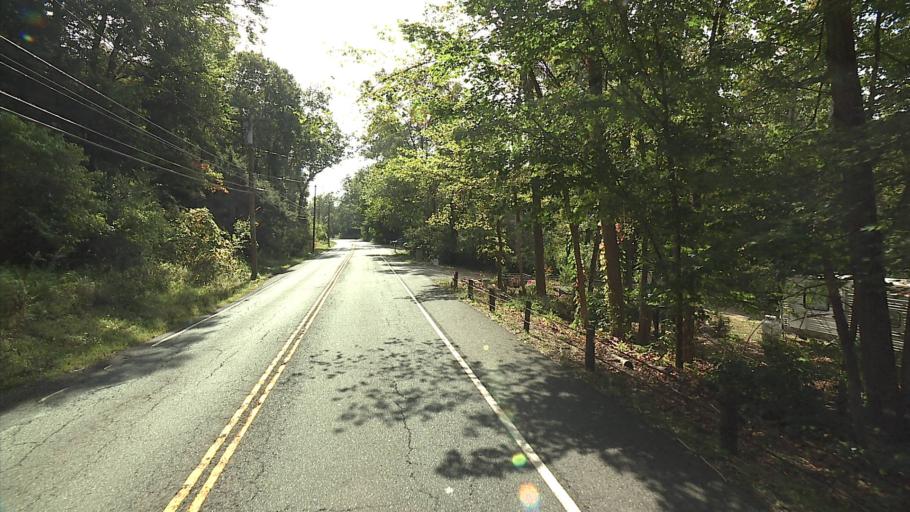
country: US
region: Connecticut
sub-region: New Haven County
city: Oxford
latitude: 41.3792
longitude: -73.1571
